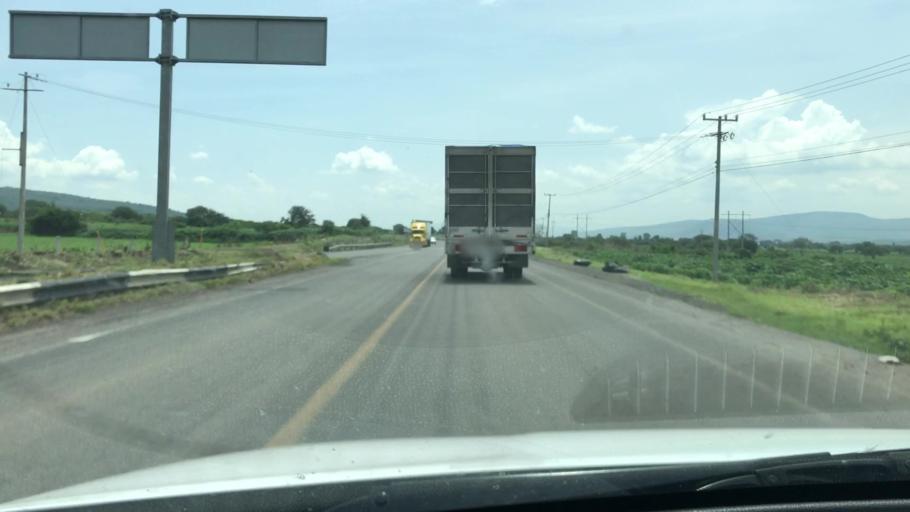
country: MX
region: Michoacan
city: Vistahermosa de Negrete
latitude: 20.2697
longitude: -102.4380
